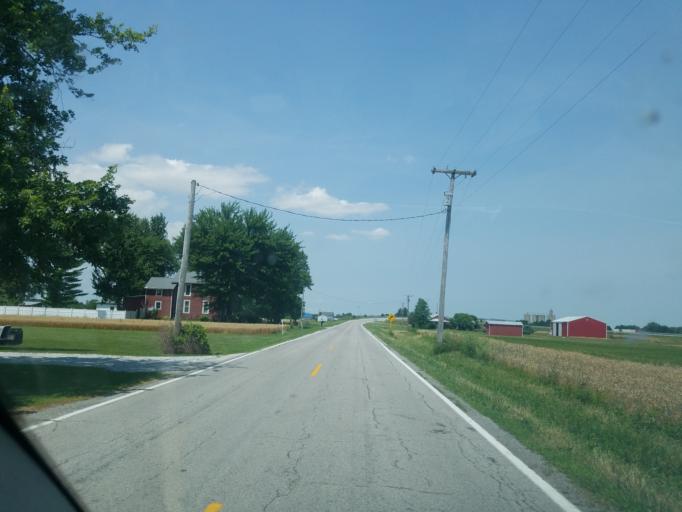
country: US
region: Ohio
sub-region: Wyandot County
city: Carey
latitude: 40.9651
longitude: -83.4859
